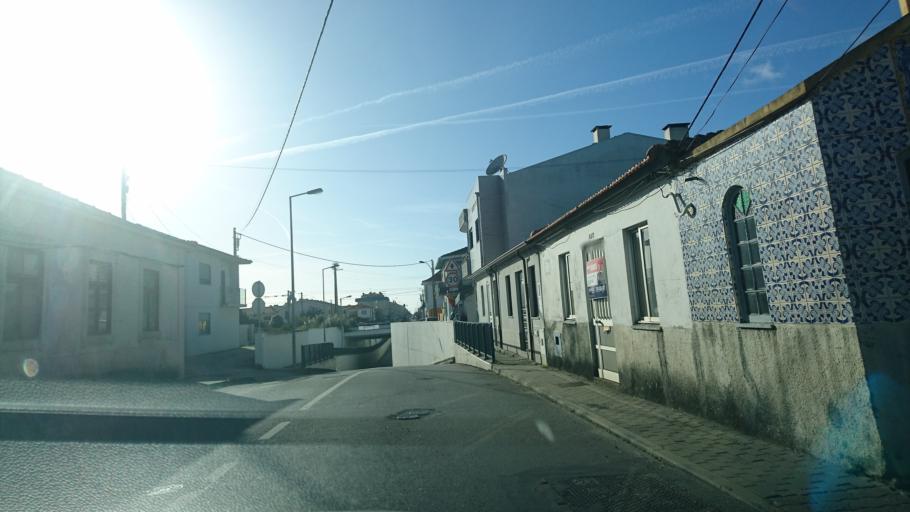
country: PT
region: Aveiro
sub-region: Ovar
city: Esmoriz
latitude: 40.9552
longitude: -8.6338
